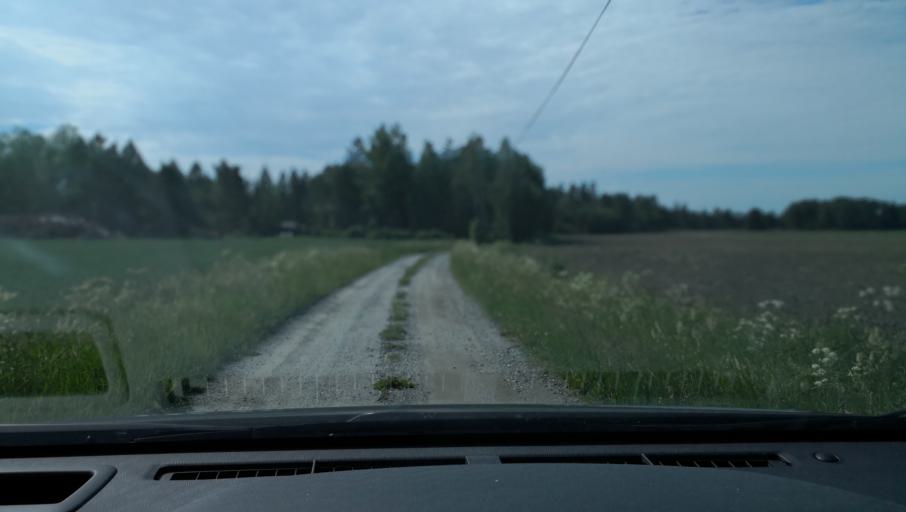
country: SE
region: Uppsala
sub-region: Enkopings Kommun
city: Enkoping
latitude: 59.7035
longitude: 17.1392
